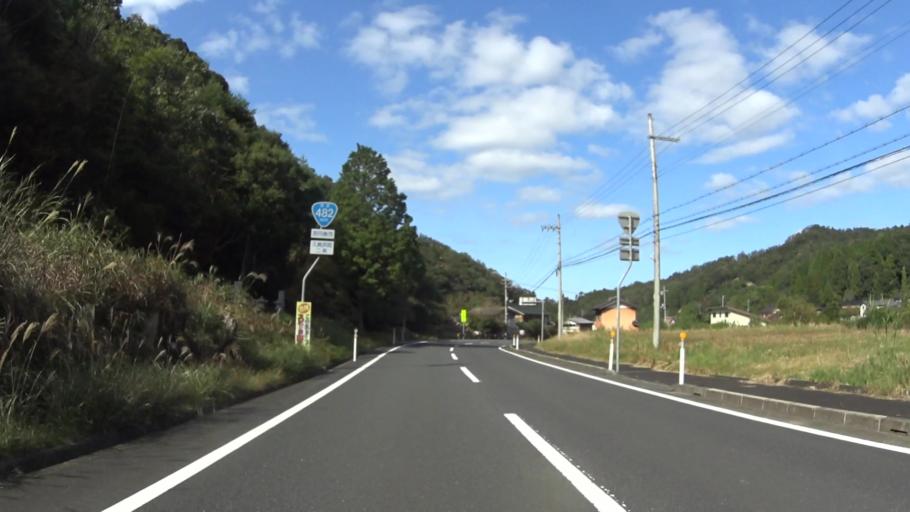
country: JP
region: Hyogo
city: Toyooka
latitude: 35.5604
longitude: 134.9790
